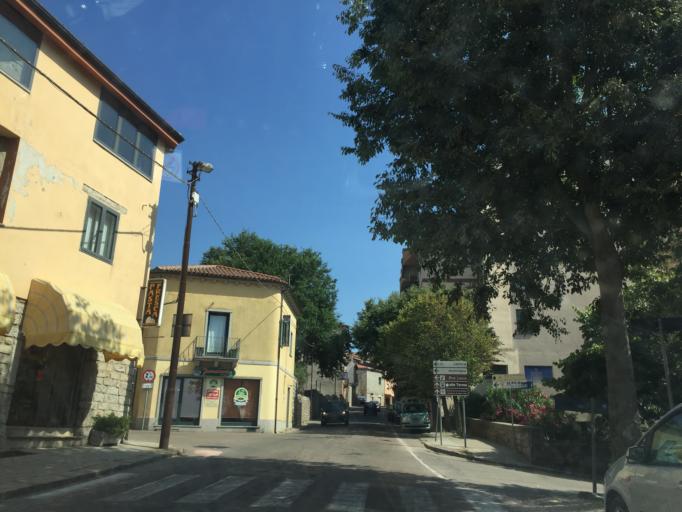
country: IT
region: Sardinia
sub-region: Provincia di Olbia-Tempio
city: Tempio Pausania
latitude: 40.9043
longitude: 9.1009
